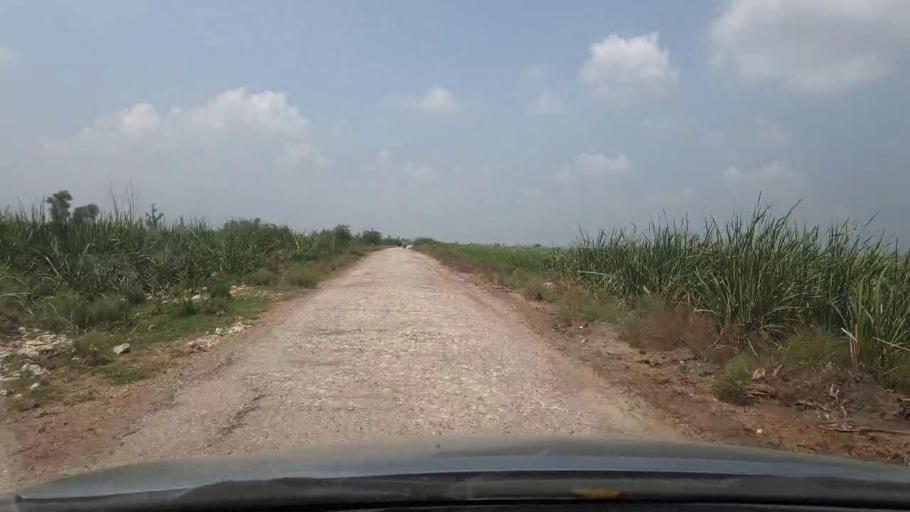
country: PK
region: Sindh
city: Khairpur
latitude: 27.4791
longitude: 68.7055
